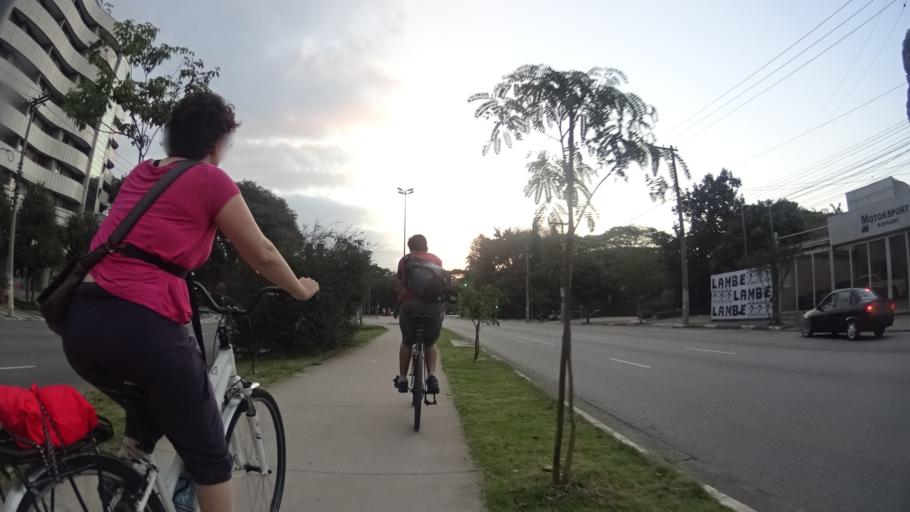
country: BR
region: Sao Paulo
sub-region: Sao Paulo
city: Sao Paulo
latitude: -23.5588
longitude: -46.6983
